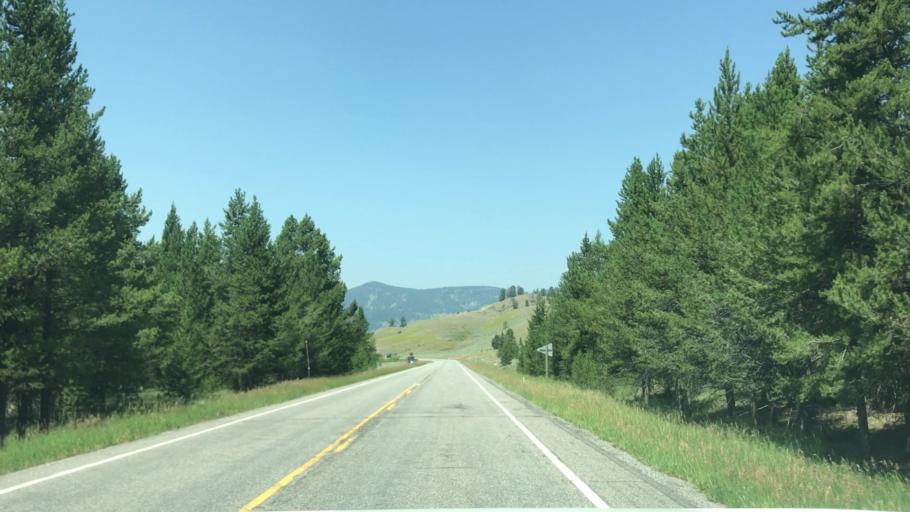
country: US
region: Montana
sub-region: Gallatin County
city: Big Sky
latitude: 45.0362
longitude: -111.1159
